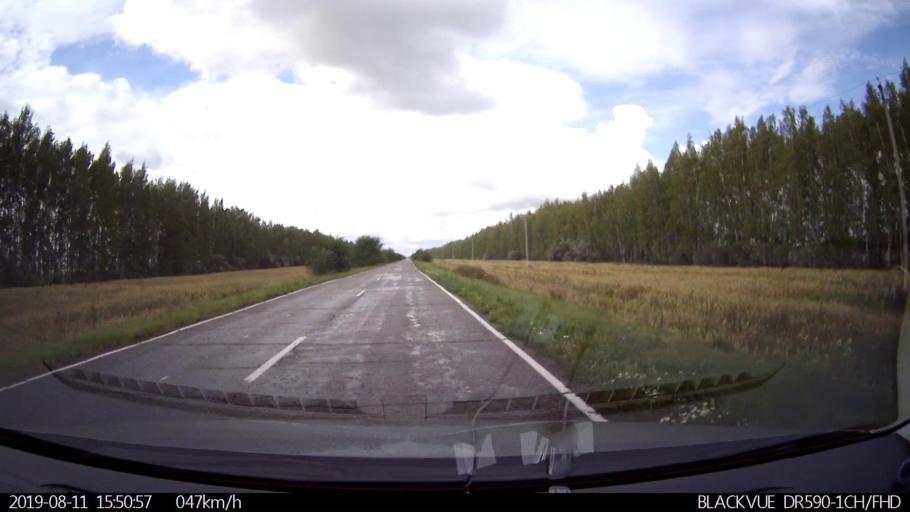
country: RU
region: Ulyanovsk
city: Ignatovka
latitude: 53.9151
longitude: 47.6559
